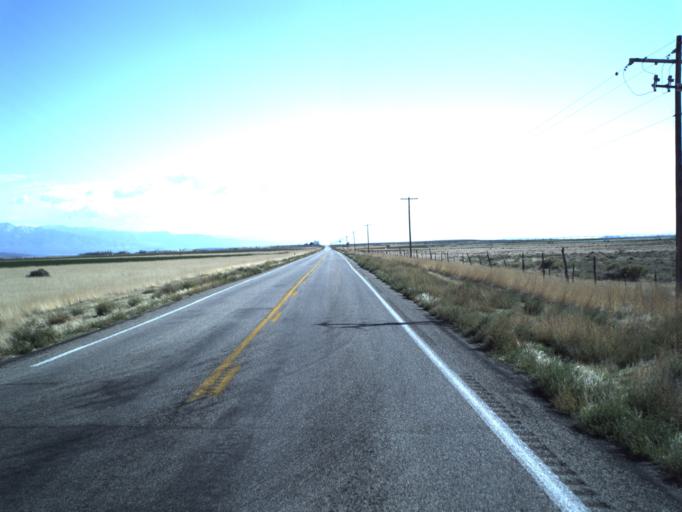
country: US
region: Utah
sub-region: Millard County
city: Delta
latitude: 39.1993
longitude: -112.4100
